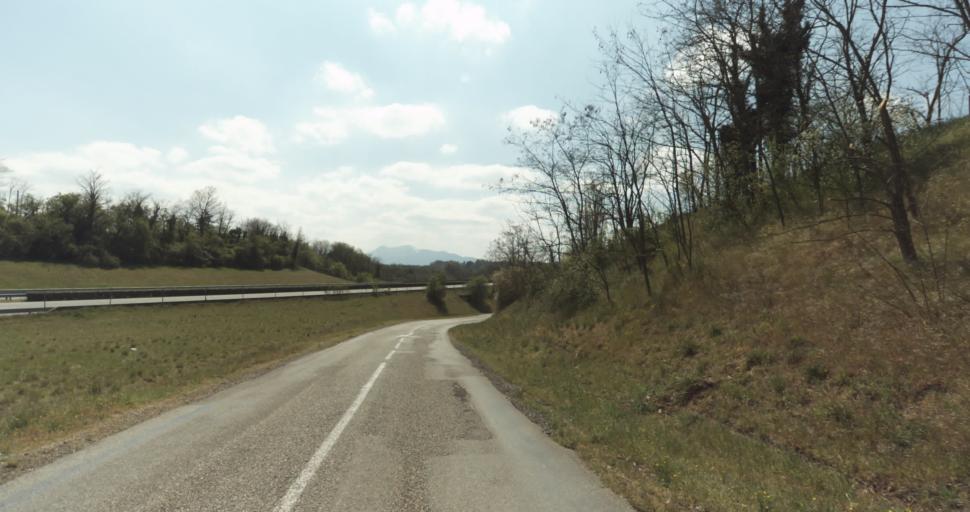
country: FR
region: Rhone-Alpes
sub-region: Departement de l'Isere
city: Saint-Marcellin
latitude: 45.1400
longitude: 5.3336
